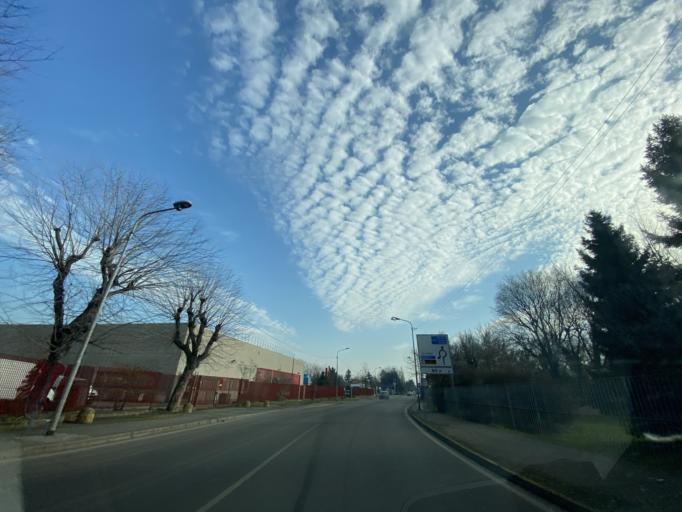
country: IT
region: Lombardy
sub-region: Citta metropolitana di Milano
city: Rozzano
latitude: 45.3837
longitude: 9.1741
